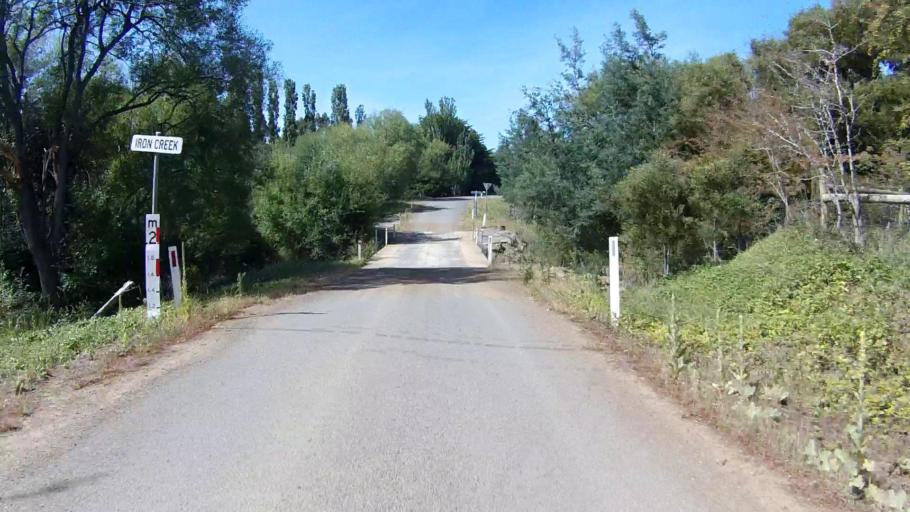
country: AU
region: Tasmania
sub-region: Sorell
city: Sorell
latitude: -42.7522
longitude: 147.6263
